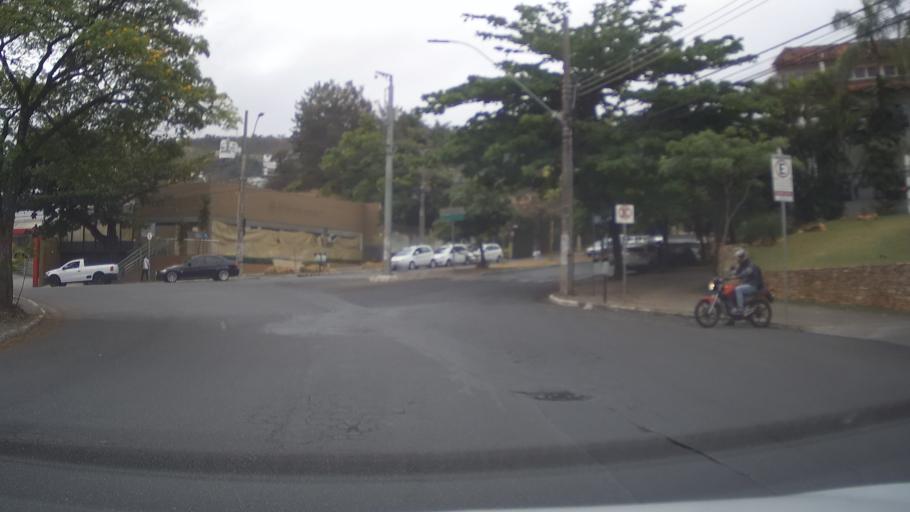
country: BR
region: Minas Gerais
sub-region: Belo Horizonte
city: Belo Horizonte
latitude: -19.9493
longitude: -43.9202
